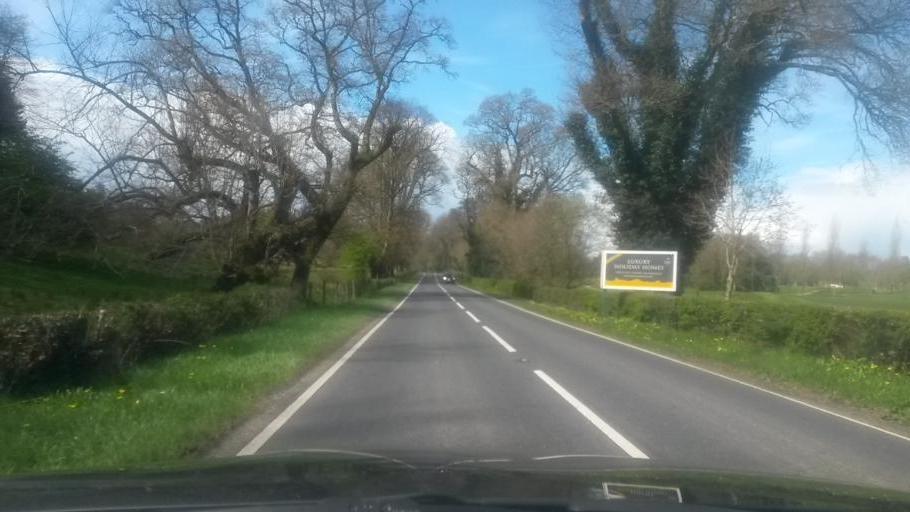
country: GB
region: Northern Ireland
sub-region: Fermanagh District
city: Enniskillen
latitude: 54.3879
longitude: -7.6979
